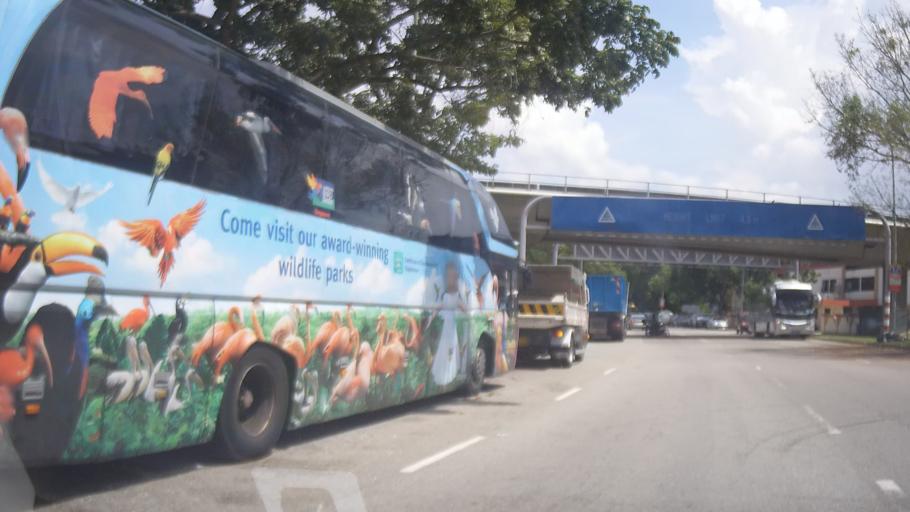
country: MY
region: Johor
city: Johor Bahru
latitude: 1.4068
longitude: 103.7503
